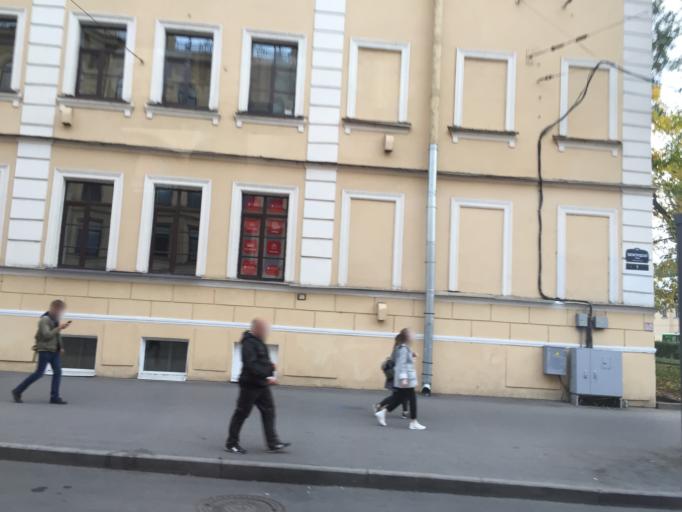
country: RU
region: St.-Petersburg
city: Centralniy
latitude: 59.9229
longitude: 30.3357
